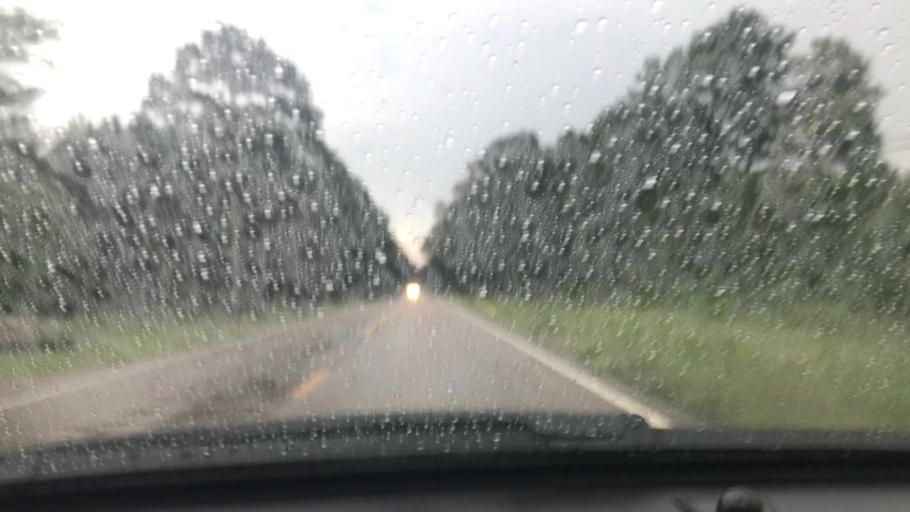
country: US
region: Mississippi
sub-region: Pike County
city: Summit
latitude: 31.2956
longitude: -90.5024
